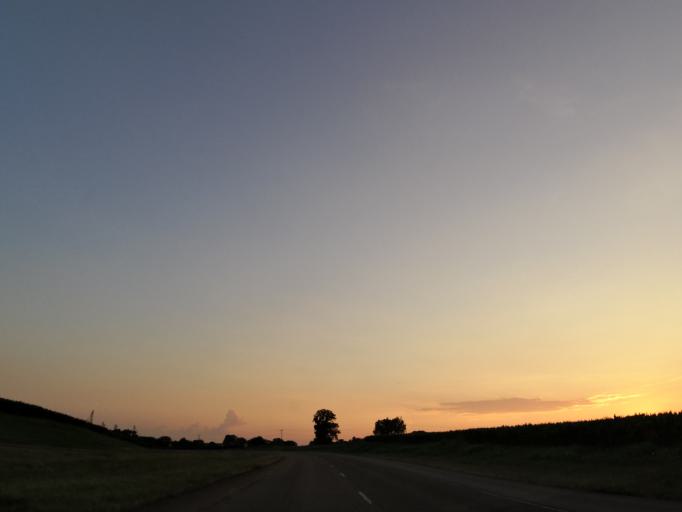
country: US
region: Tennessee
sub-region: Carroll County
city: McKenzie
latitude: 36.1960
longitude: -88.4223
